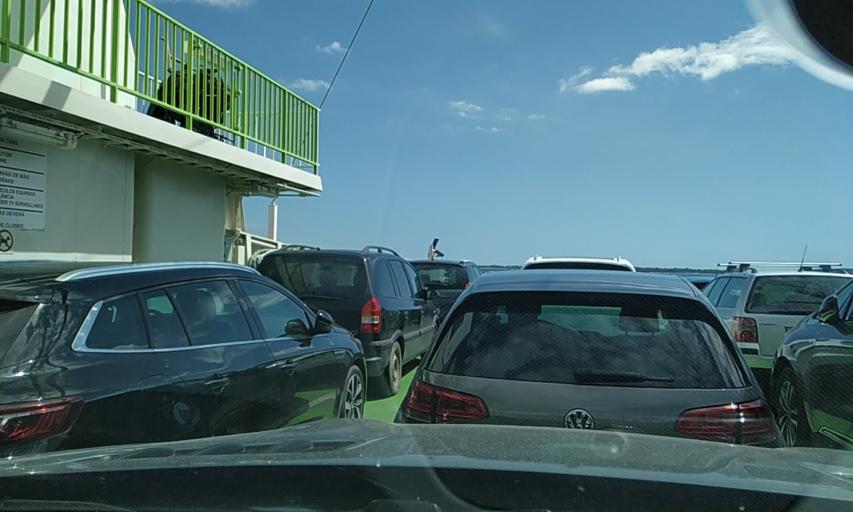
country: PT
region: Setubal
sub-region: Setubal
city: Setubal
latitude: 38.5133
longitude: -8.8857
